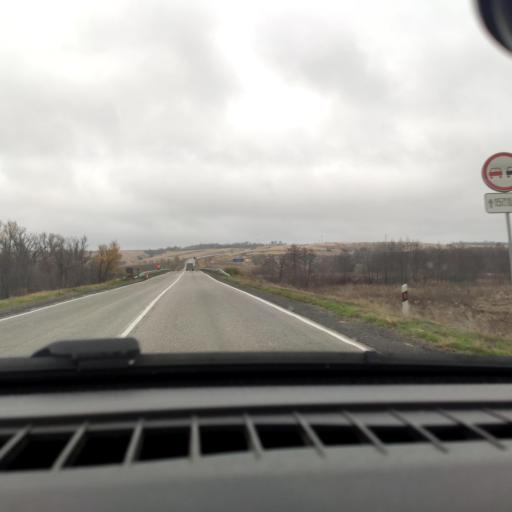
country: RU
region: Voronezj
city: Uryv-Pokrovka
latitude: 51.1294
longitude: 39.0427
